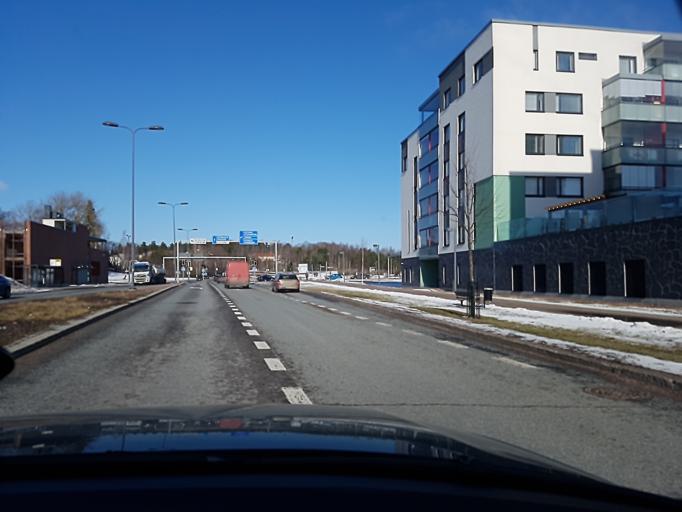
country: FI
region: Uusimaa
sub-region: Helsinki
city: Kirkkonummi
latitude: 60.1228
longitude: 24.4418
